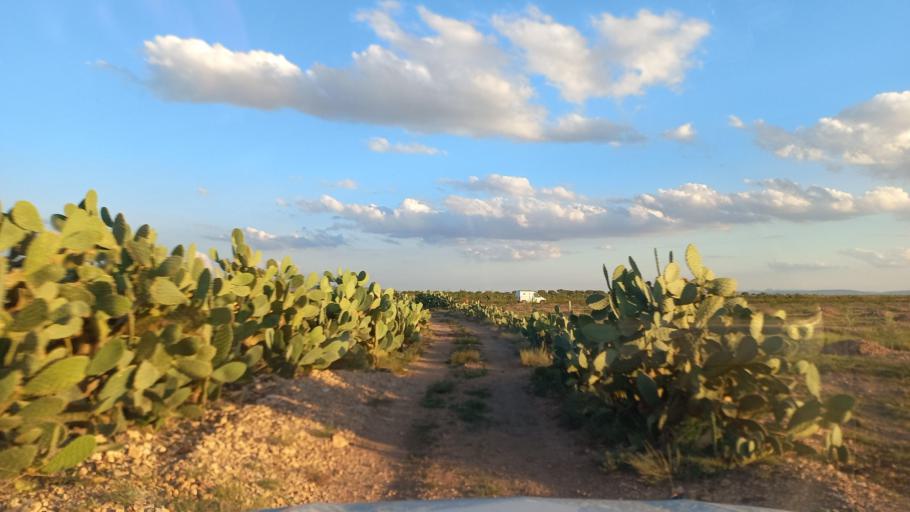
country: TN
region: Al Qasrayn
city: Sbiba
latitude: 35.3753
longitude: 9.0520
